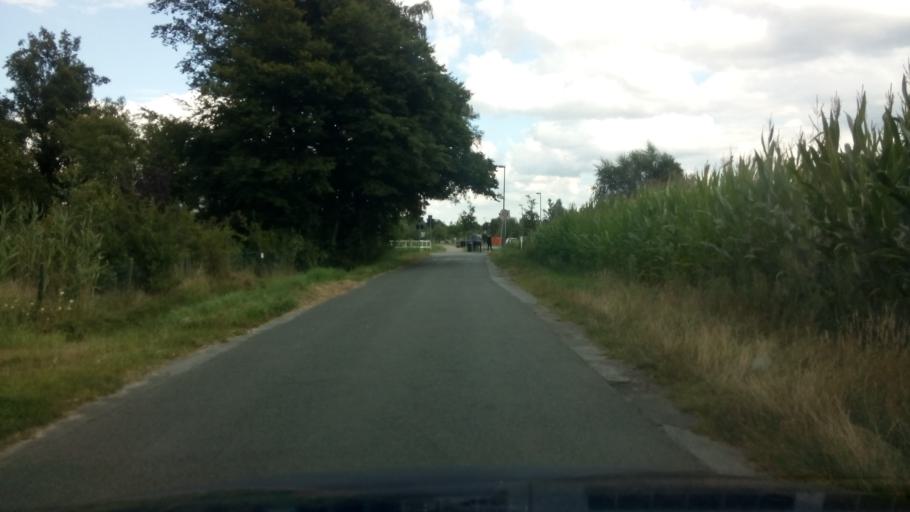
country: DE
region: Lower Saxony
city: Lilienthal
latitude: 53.1295
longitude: 8.8919
